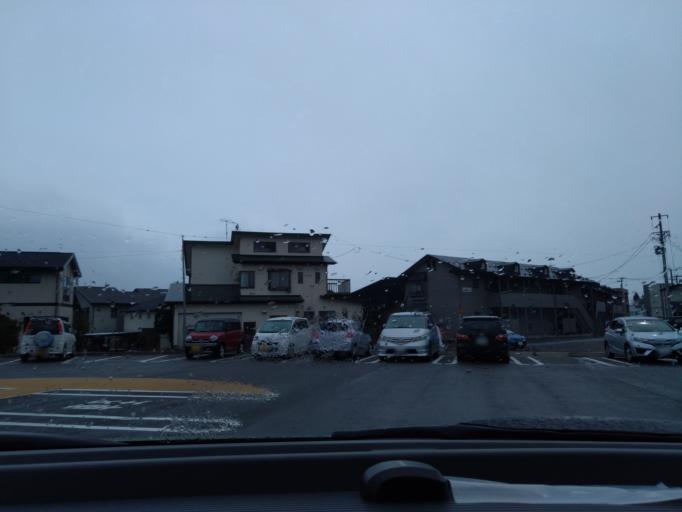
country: JP
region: Iwate
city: Morioka-shi
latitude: 39.7215
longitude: 141.1402
